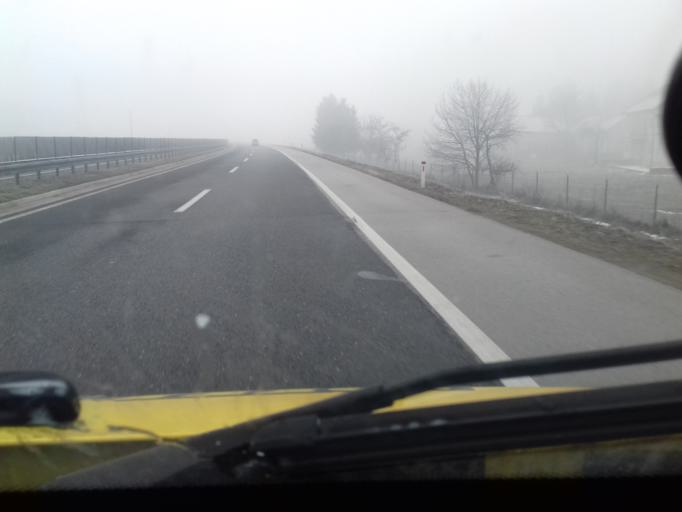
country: BA
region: Federation of Bosnia and Herzegovina
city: Mahala
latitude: 43.9793
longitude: 18.2351
